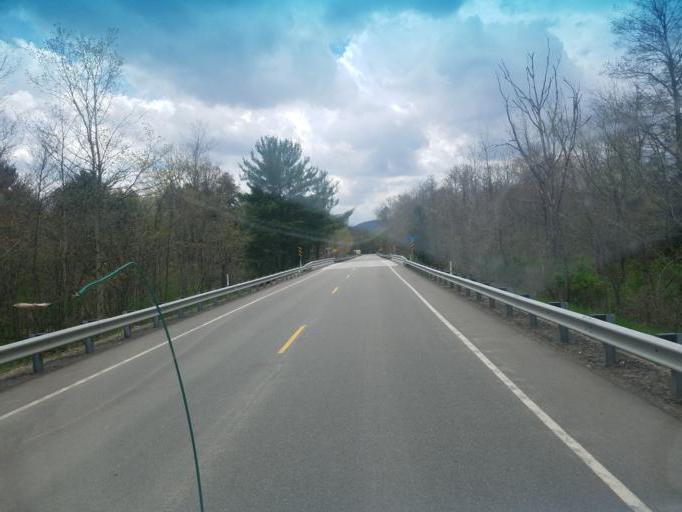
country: US
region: New York
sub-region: Allegany County
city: Wellsville
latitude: 41.9972
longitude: -77.8642
